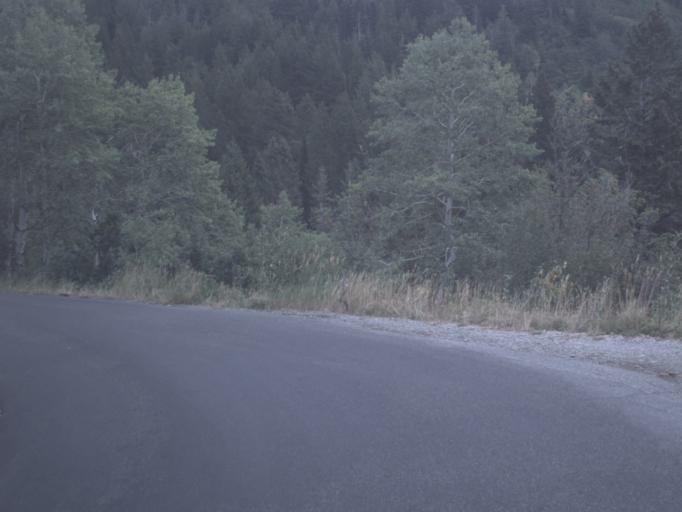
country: US
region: Utah
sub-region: Utah County
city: Lindon
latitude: 40.4087
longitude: -111.6041
